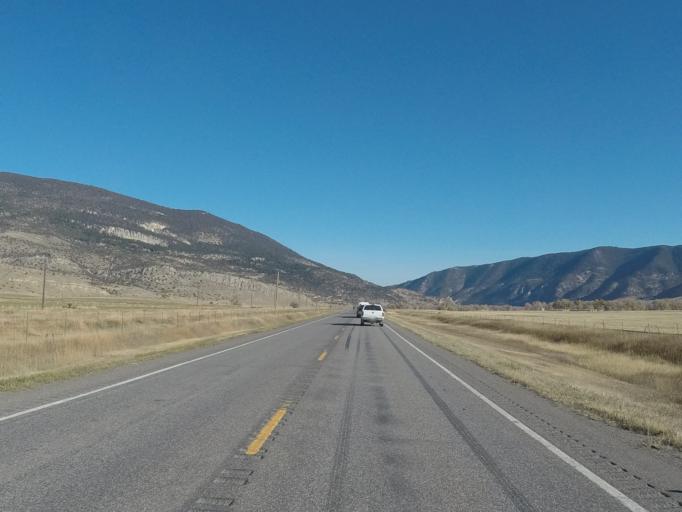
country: US
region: Montana
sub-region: Park County
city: Livingston
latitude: 45.5549
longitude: -110.5956
